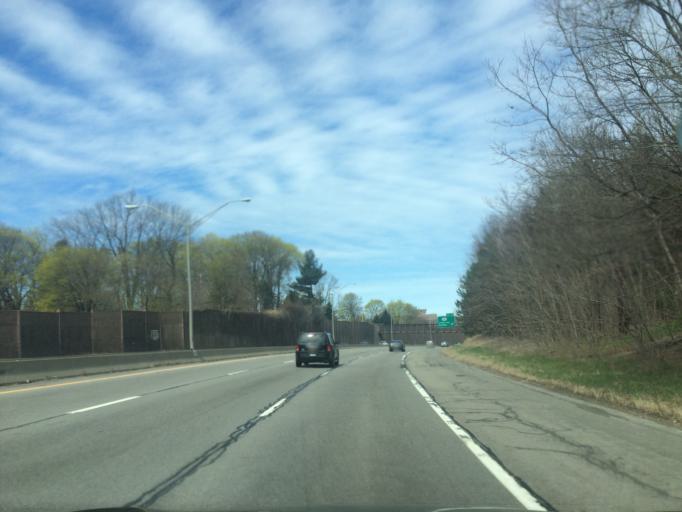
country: US
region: New York
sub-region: Monroe County
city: Pittsford
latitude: 43.1242
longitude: -77.5229
